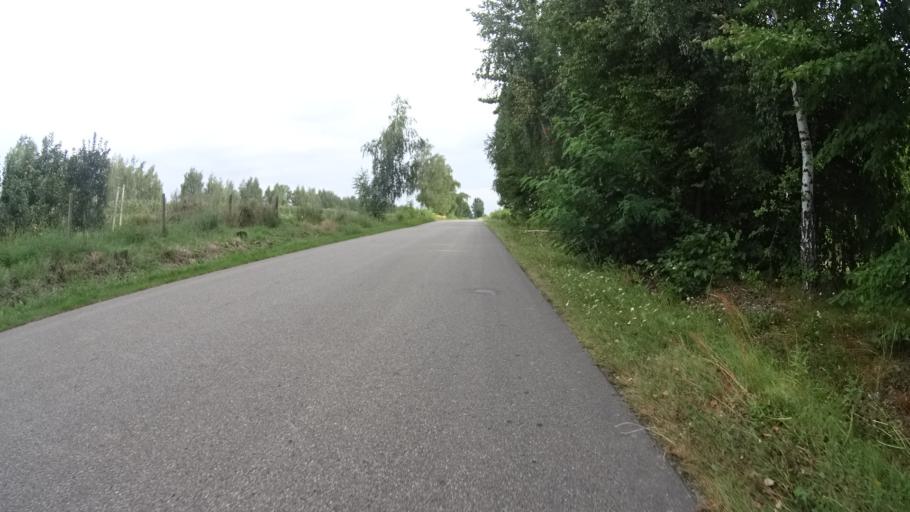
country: PL
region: Masovian Voivodeship
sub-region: Powiat grojecki
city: Goszczyn
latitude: 51.6995
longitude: 20.8555
